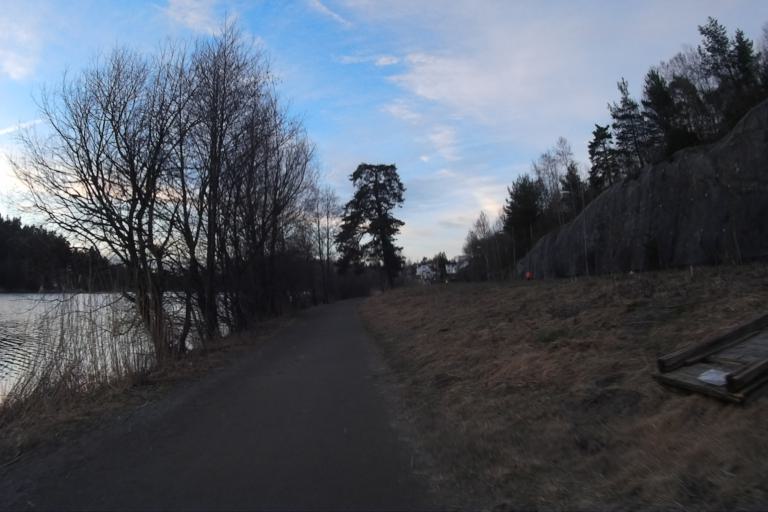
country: NO
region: Oslo
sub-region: Oslo
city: Oslo
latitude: 59.8942
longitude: 10.8325
